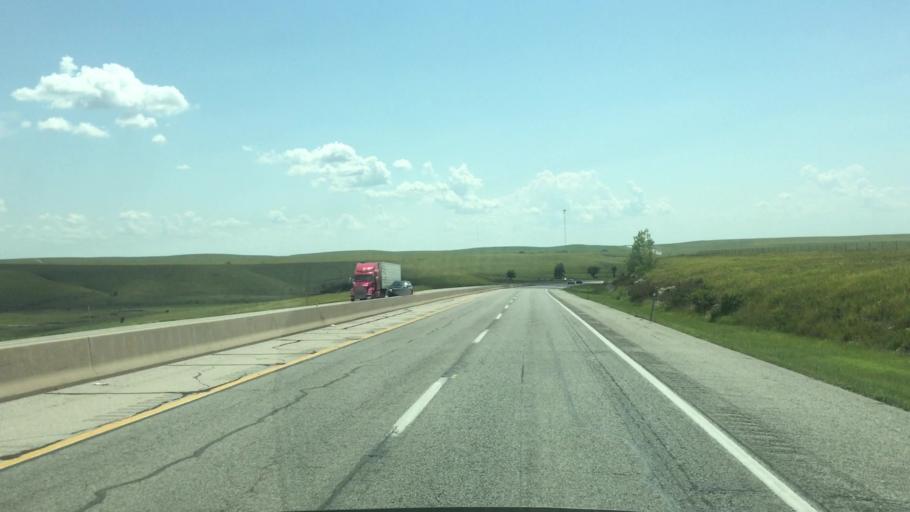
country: US
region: Kansas
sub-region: Chase County
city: Cottonwood Falls
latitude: 38.1808
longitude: -96.4620
